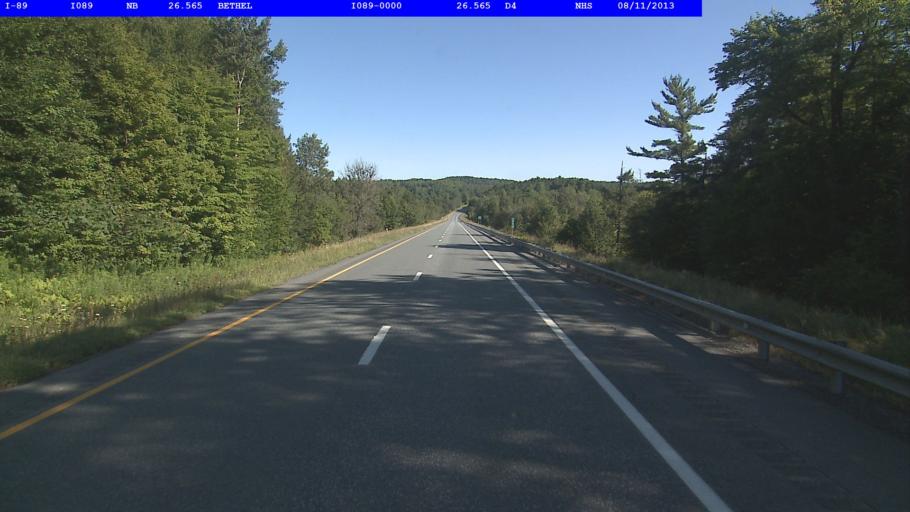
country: US
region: Vermont
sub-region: Orange County
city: Randolph
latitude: 43.8831
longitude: -72.6156
